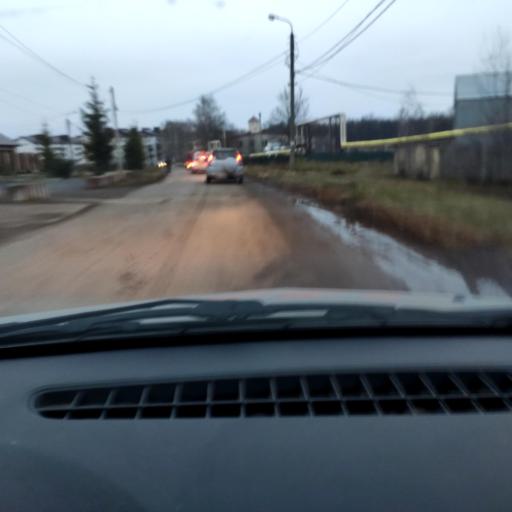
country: RU
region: Bashkortostan
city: Ufa
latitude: 54.6713
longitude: 55.9101
